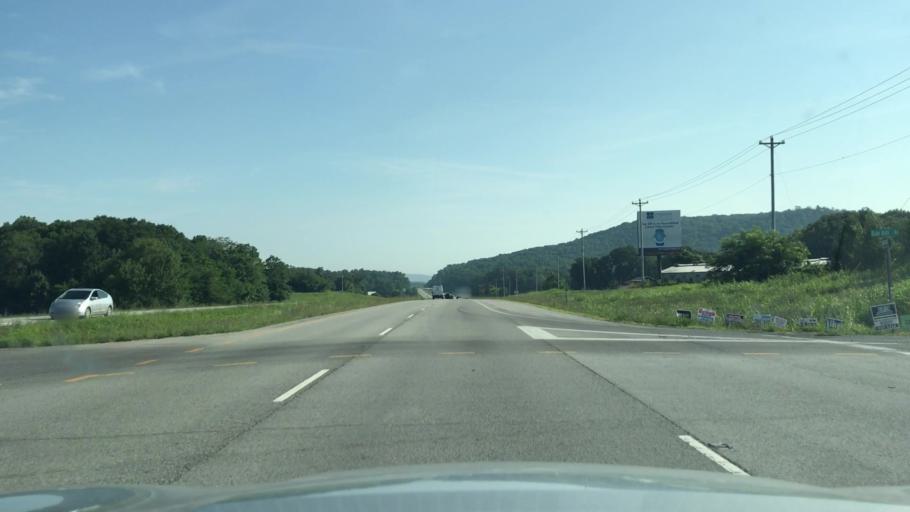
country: US
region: Tennessee
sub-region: Overton County
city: Livingston
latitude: 36.2971
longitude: -85.3699
